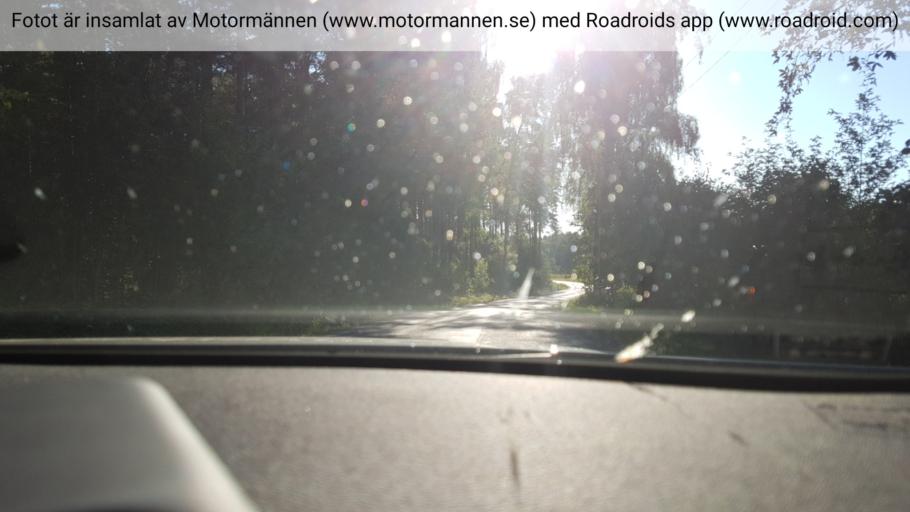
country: SE
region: Vaestra Goetaland
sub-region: Tidaholms Kommun
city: Tidaholm
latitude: 58.1375
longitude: 13.9654
